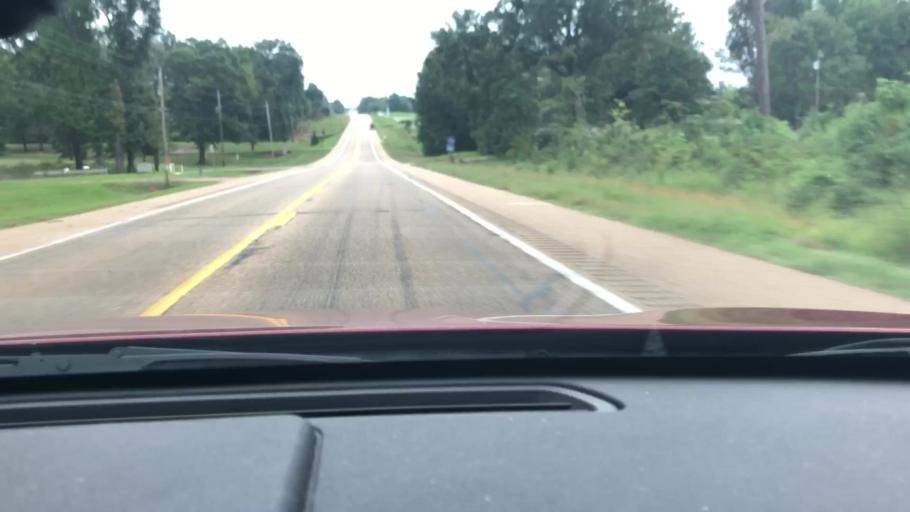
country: US
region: Arkansas
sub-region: Miller County
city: Texarkana
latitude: 33.4290
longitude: -93.9357
